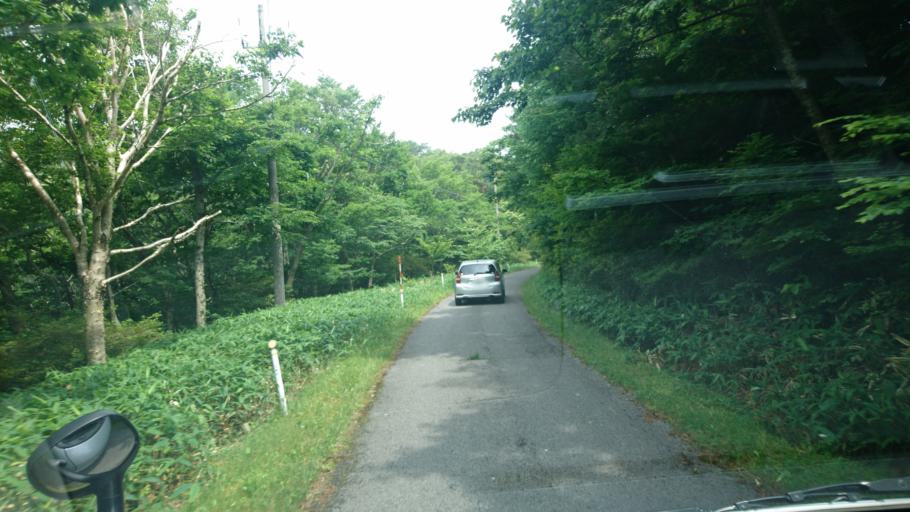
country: JP
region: Iwate
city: Ofunato
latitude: 39.1506
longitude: 141.7541
